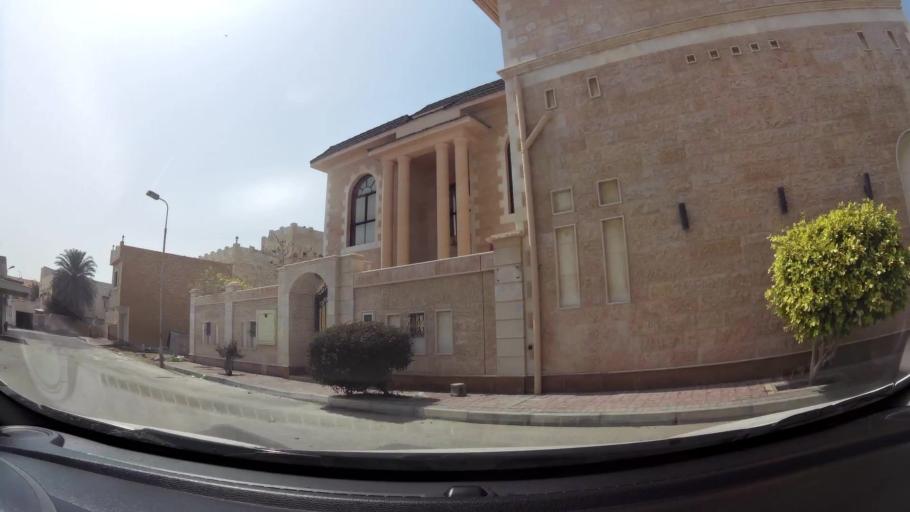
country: BH
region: Manama
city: Jidd Hafs
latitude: 26.2159
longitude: 50.4487
